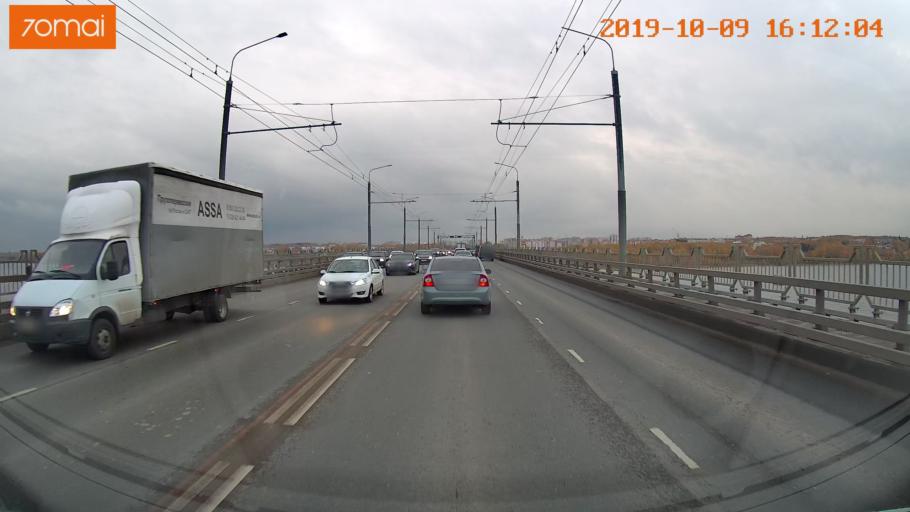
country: RU
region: Kostroma
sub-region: Kostromskoy Rayon
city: Kostroma
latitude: 57.7525
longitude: 40.9387
